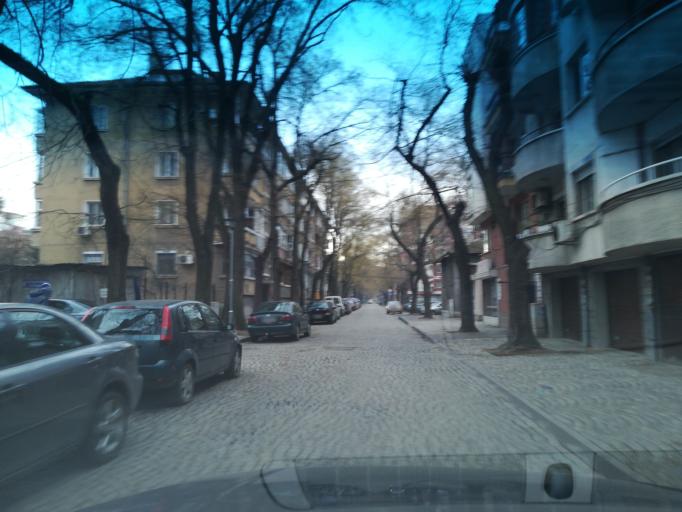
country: BG
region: Plovdiv
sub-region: Obshtina Plovdiv
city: Plovdiv
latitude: 42.1397
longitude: 24.7596
